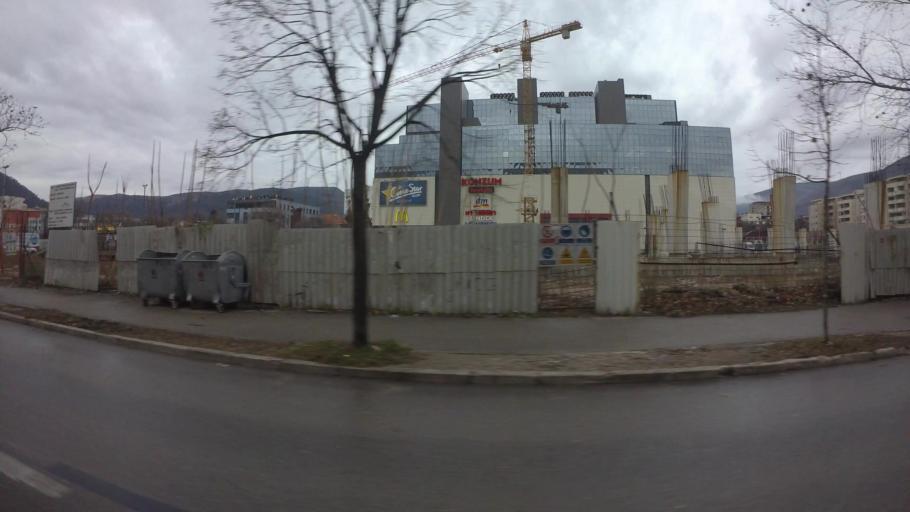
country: BA
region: Federation of Bosnia and Herzegovina
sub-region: Hercegovacko-Bosanski Kanton
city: Mostar
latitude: 43.3485
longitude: 17.8067
